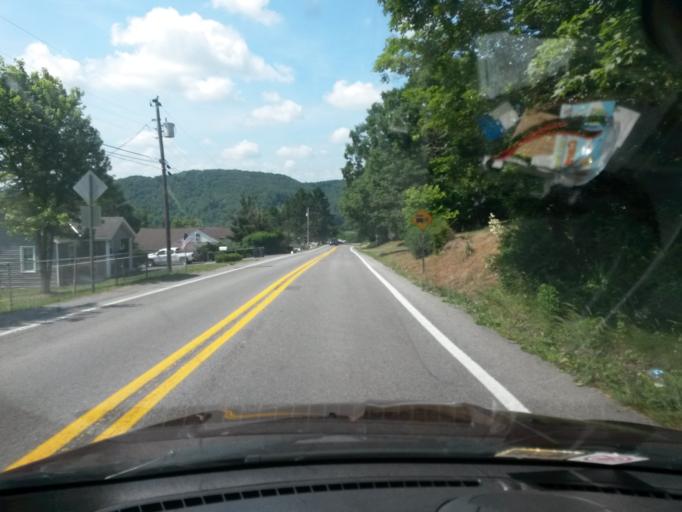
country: US
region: West Virginia
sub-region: Mercer County
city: Princeton
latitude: 37.3908
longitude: -81.1178
